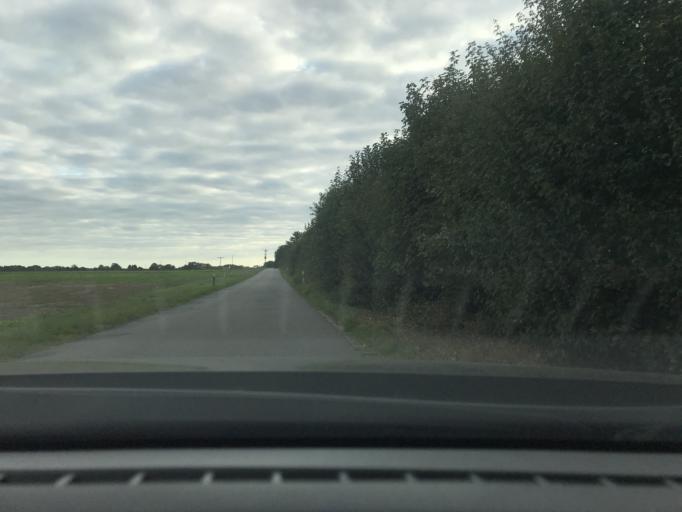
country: DE
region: Lower Saxony
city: Suderburg
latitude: 52.9085
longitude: 10.4549
